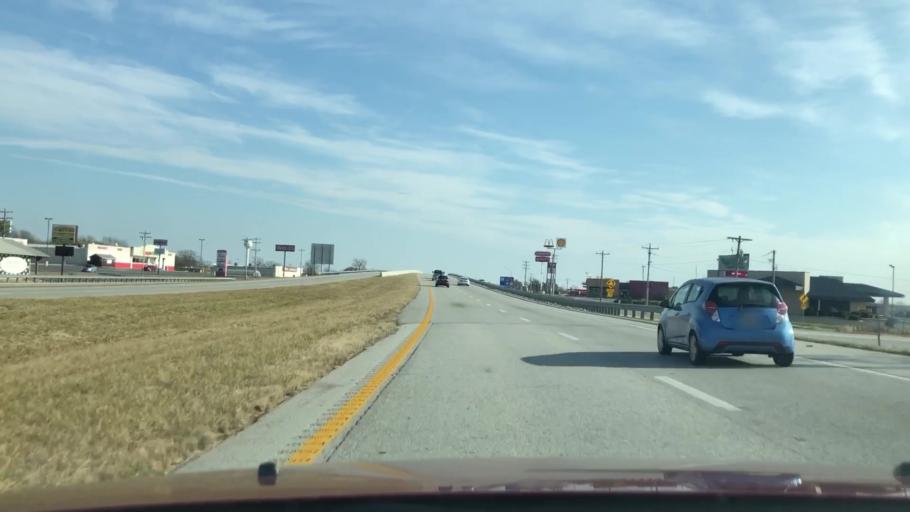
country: US
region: Missouri
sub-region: Webster County
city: Rogersville
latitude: 37.1096
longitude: -93.0612
